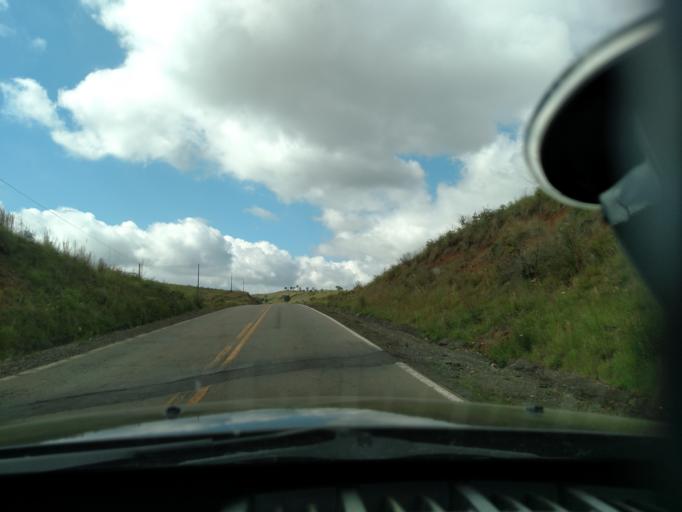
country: BR
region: Santa Catarina
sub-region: Lages
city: Lages
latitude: -27.8712
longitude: -50.1805
